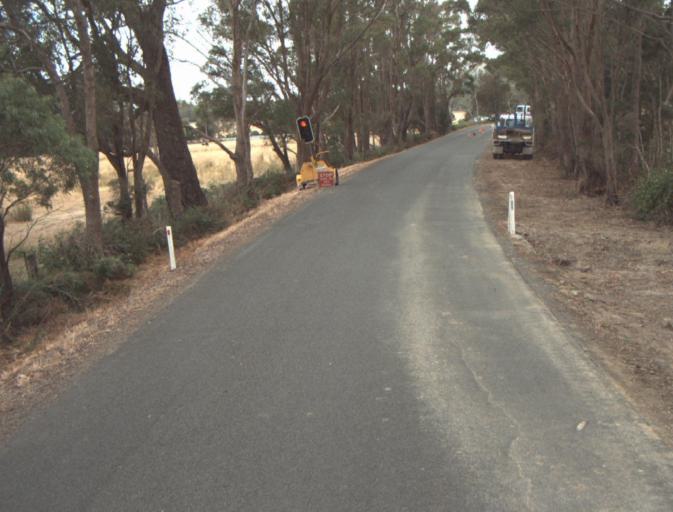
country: AU
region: Tasmania
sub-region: Launceston
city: Mayfield
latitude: -41.2253
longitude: 147.0313
